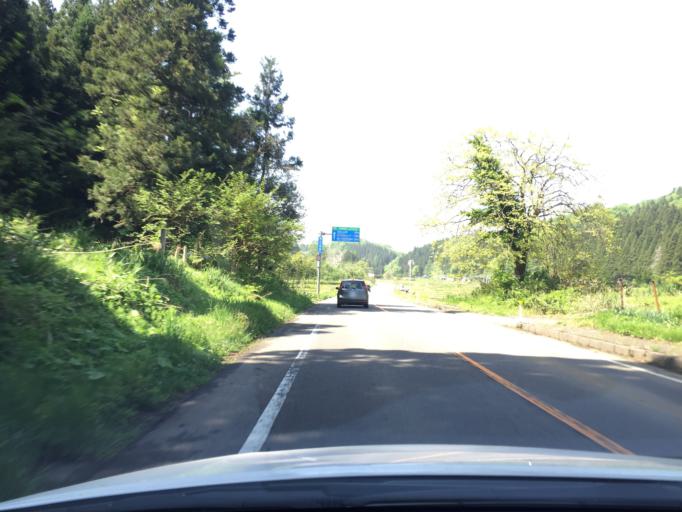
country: JP
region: Niigata
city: Muramatsu
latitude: 37.6490
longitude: 139.1307
